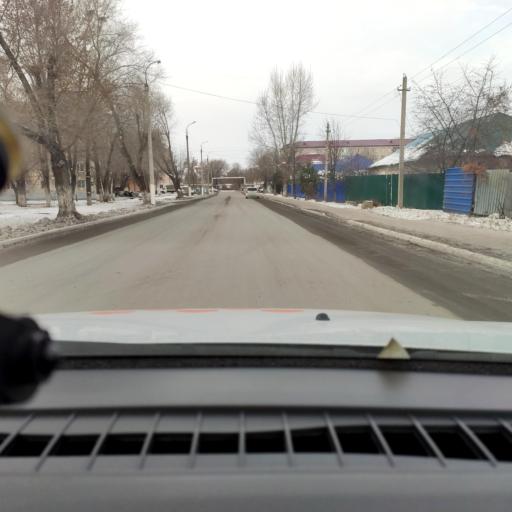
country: RU
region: Samara
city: Chapayevsk
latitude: 52.9596
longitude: 49.6886
